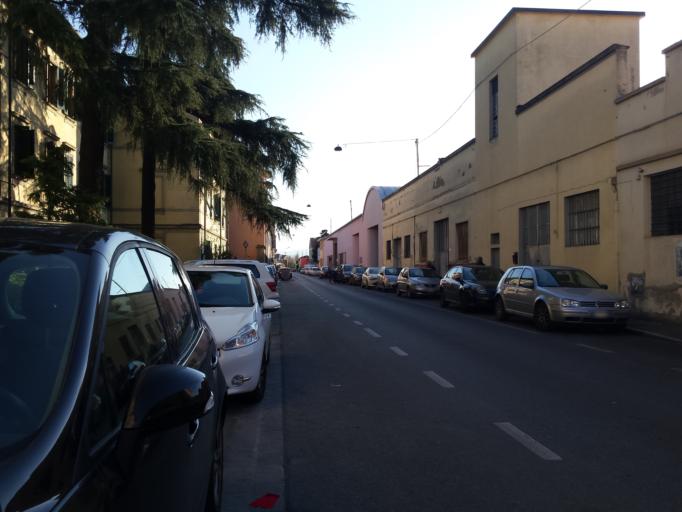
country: IT
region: Tuscany
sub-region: Provincia di Prato
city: Prato
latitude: 43.8862
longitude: 11.0814
